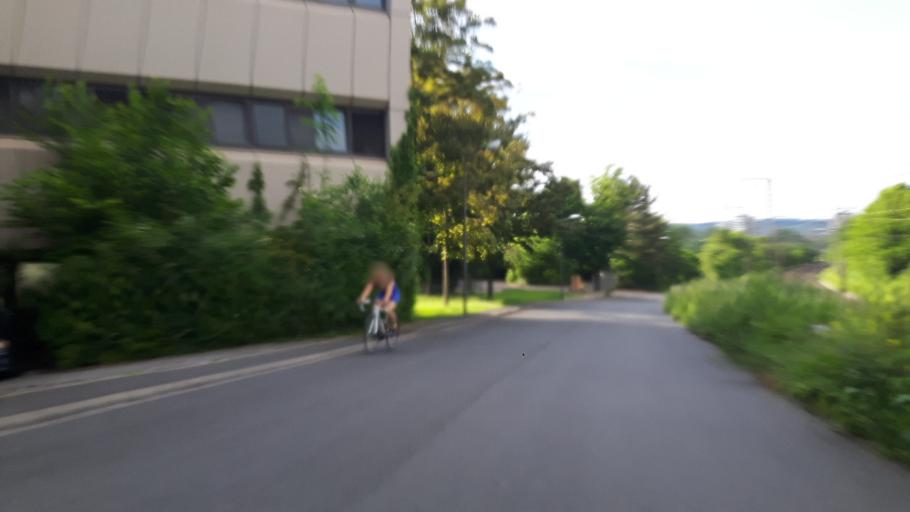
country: DE
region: Bavaria
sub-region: Regierungsbezirk Unterfranken
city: Wuerzburg
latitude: 49.7656
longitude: 9.9397
